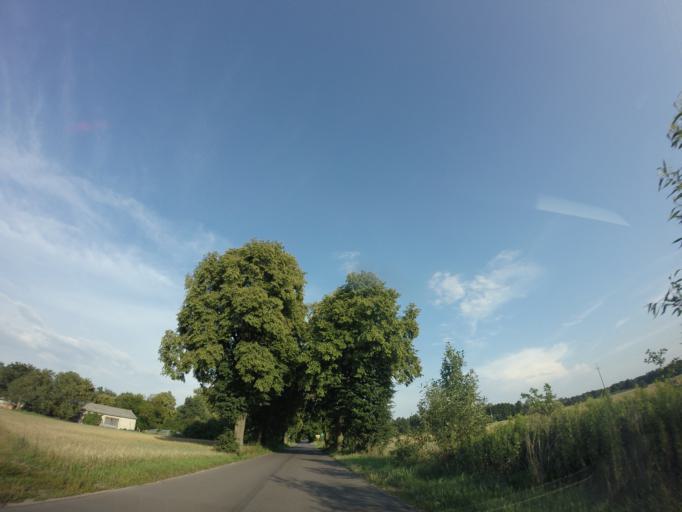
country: PL
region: Lublin Voivodeship
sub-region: Powiat pulawski
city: Kurow
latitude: 51.4262
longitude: 22.2199
